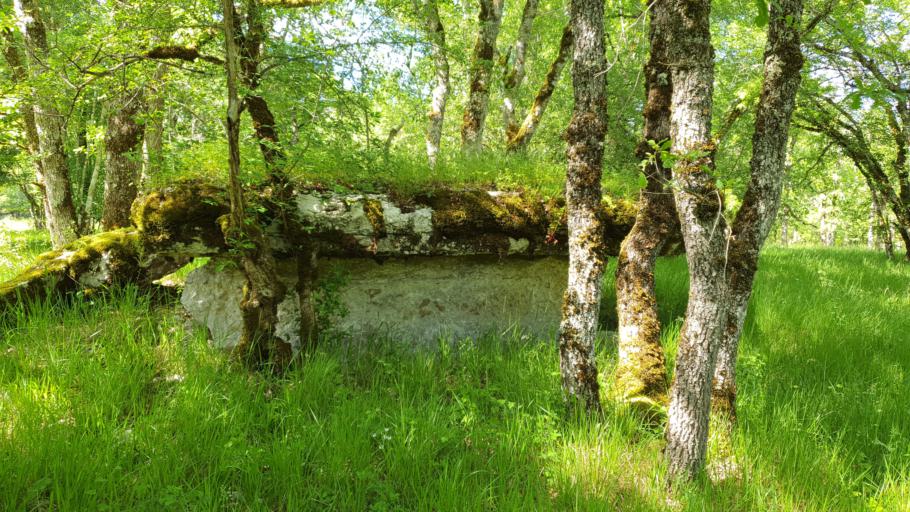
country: FR
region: Midi-Pyrenees
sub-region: Departement du Lot
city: Gramat
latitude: 44.7149
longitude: 1.7513
